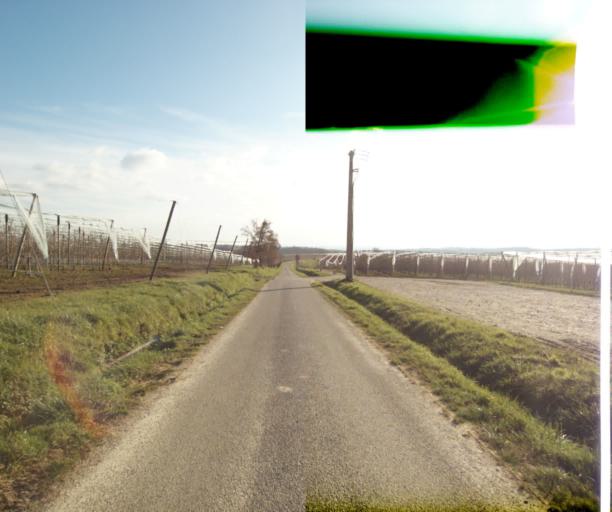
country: FR
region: Midi-Pyrenees
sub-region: Departement du Tarn-et-Garonne
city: Moissac
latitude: 44.1393
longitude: 1.0546
